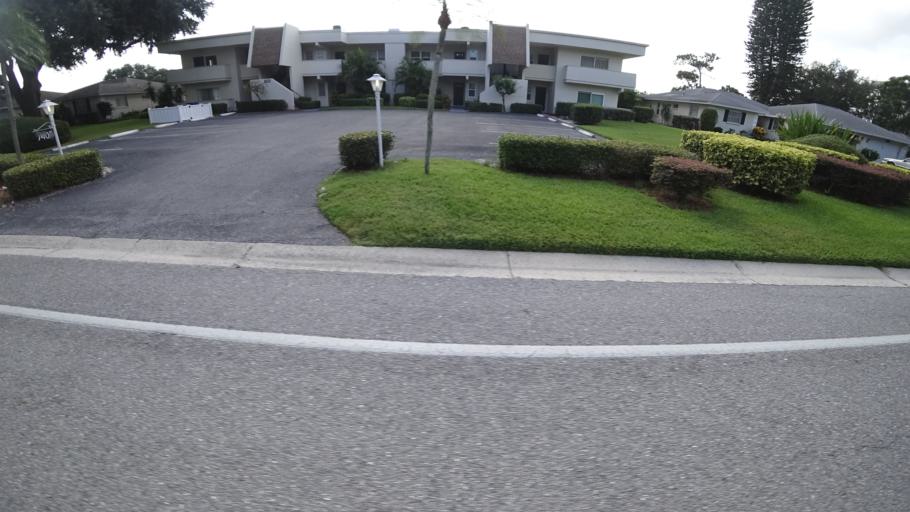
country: US
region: Florida
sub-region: Sarasota County
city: Desoto Lakes
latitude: 27.4086
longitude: -82.4967
